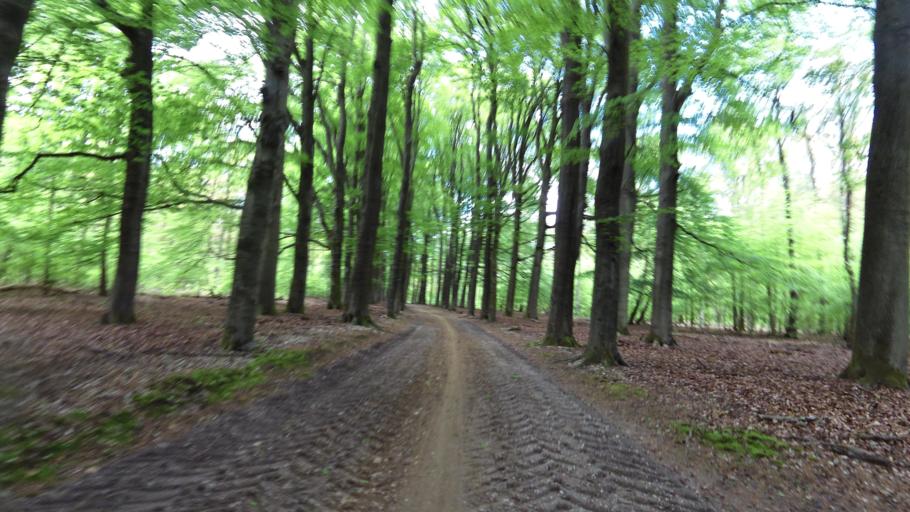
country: NL
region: Gelderland
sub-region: Gemeente Rheden
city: De Steeg
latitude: 52.0424
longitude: 6.0460
